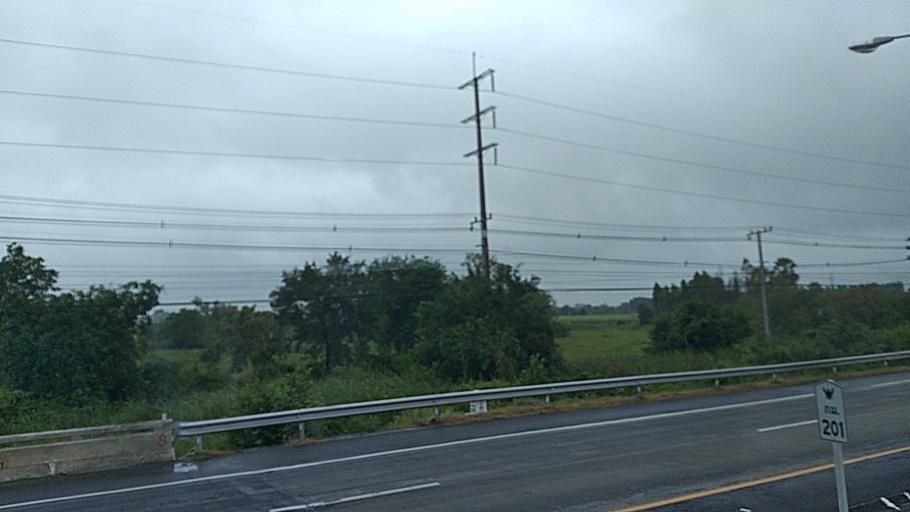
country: TH
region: Nakhon Ratchasima
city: Phimai
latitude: 15.2901
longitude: 102.4167
